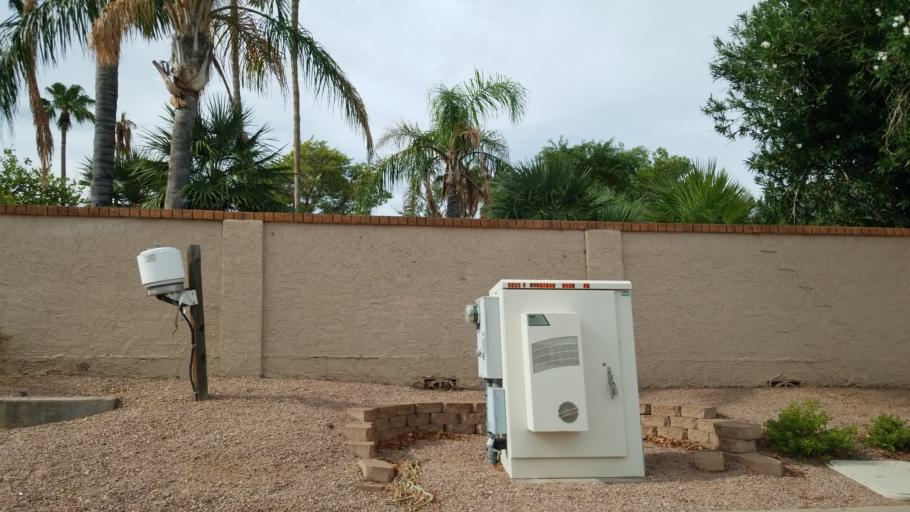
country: US
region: Arizona
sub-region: Maricopa County
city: Paradise Valley
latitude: 33.5736
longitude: -111.8996
